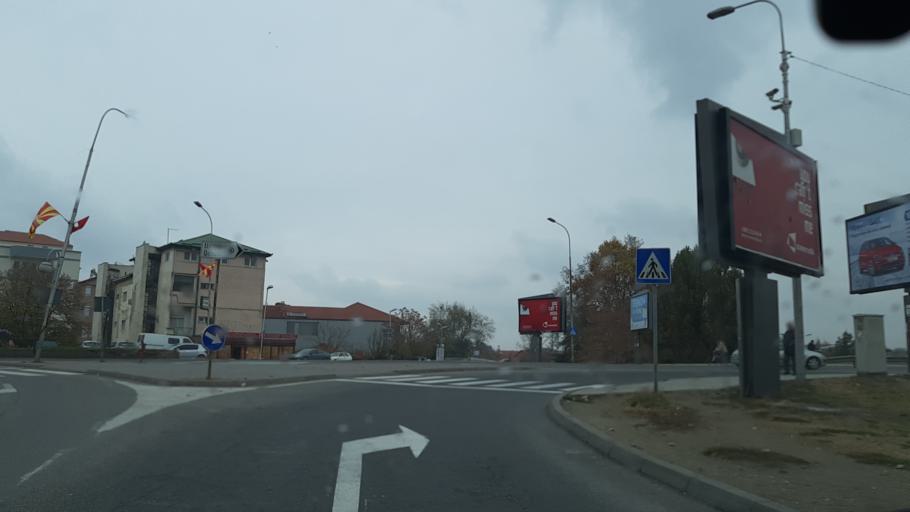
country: MK
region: Cair
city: Cair
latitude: 42.0056
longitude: 21.4406
